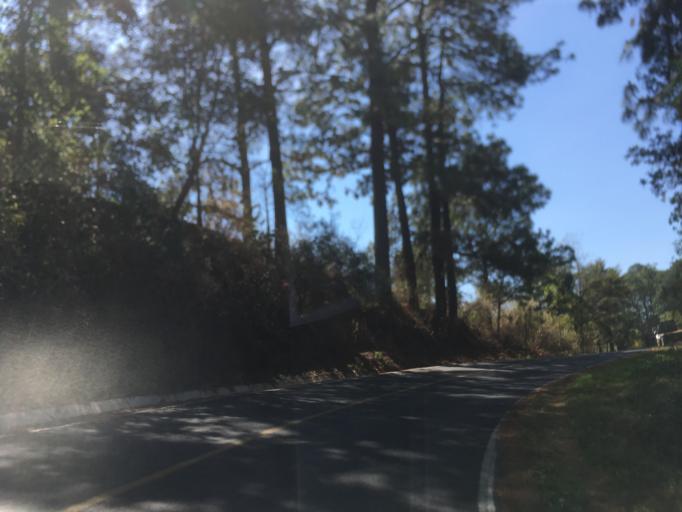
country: MX
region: Michoacan
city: Tzitzio
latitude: 19.6517
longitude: -100.9409
